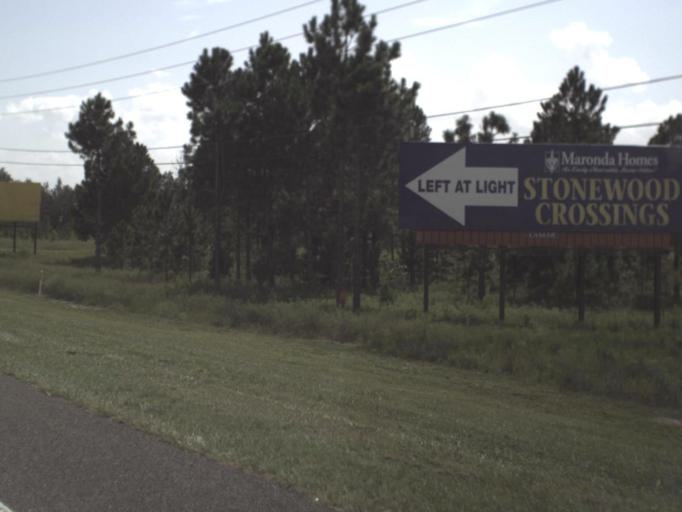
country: US
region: Florida
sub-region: Polk County
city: Davenport
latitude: 28.1478
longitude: -81.6389
